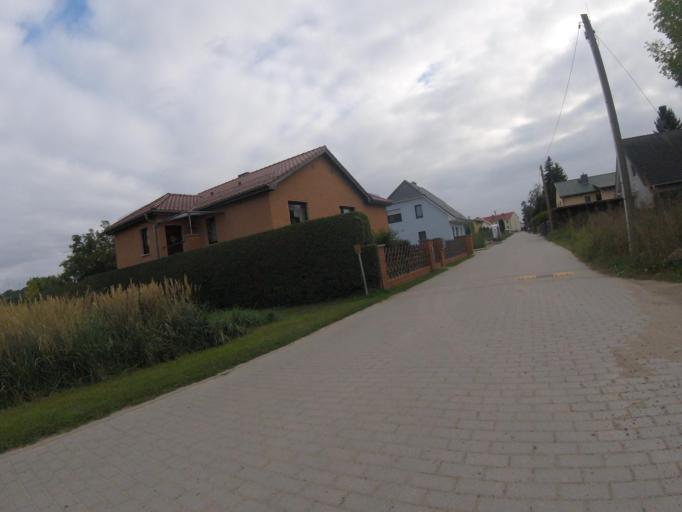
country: DE
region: Brandenburg
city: Mittenwalde
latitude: 52.2699
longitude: 13.5304
